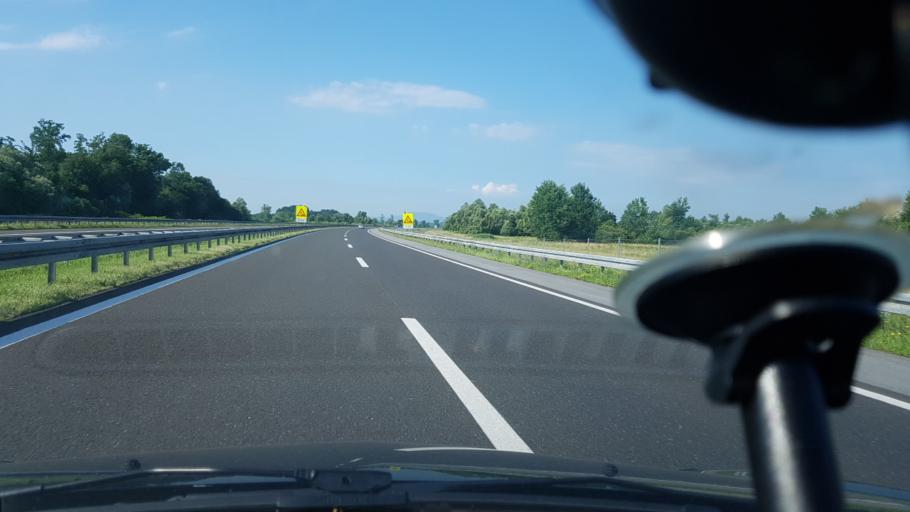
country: HR
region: Zagrebacka
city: Jakovlje
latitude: 45.9702
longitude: 15.8517
